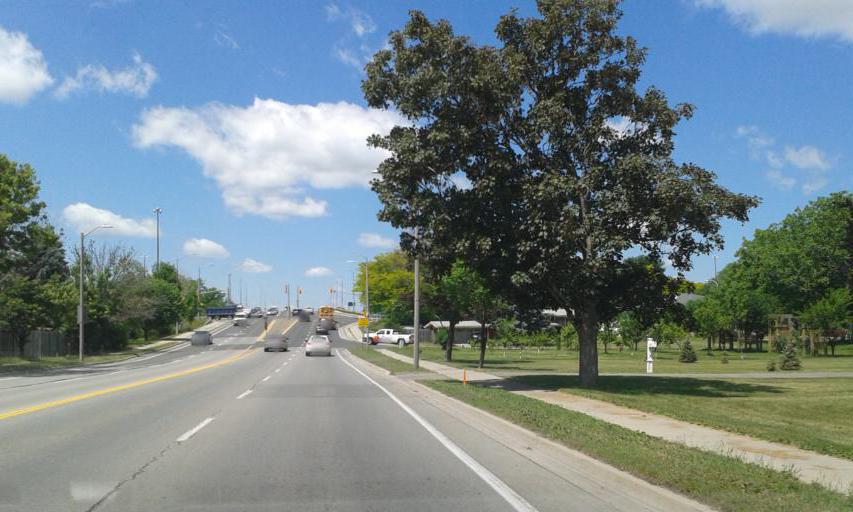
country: CA
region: Ontario
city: Niagara Falls
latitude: 43.1149
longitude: -79.1157
